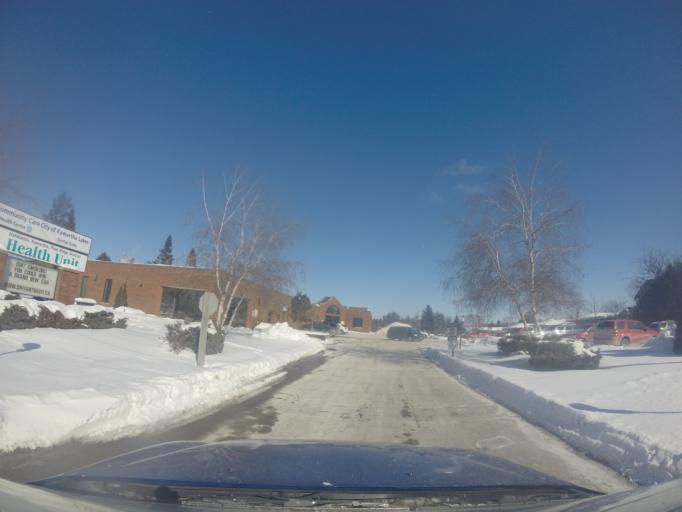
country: CA
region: Ontario
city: Omemee
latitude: 44.3437
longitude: -78.7475
